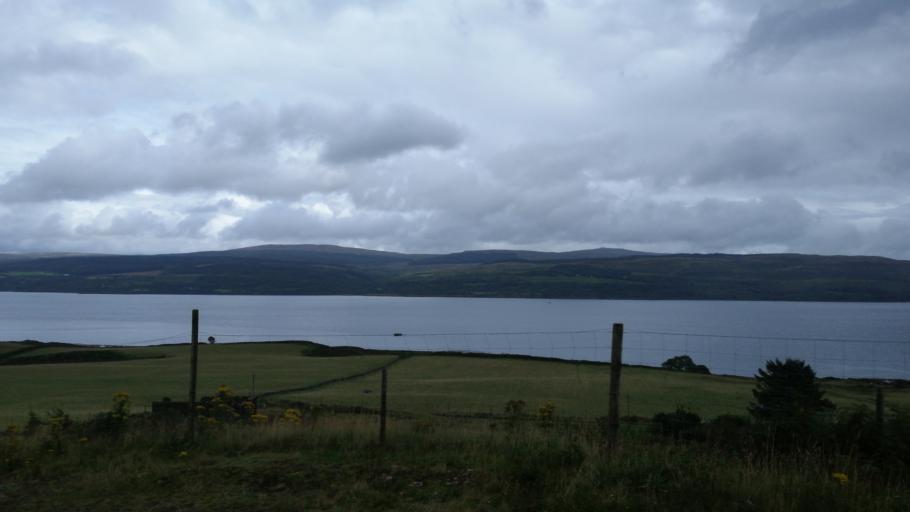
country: GB
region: Scotland
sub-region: Argyll and Bute
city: Isle Of Mull
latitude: 56.5542
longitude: -5.9801
